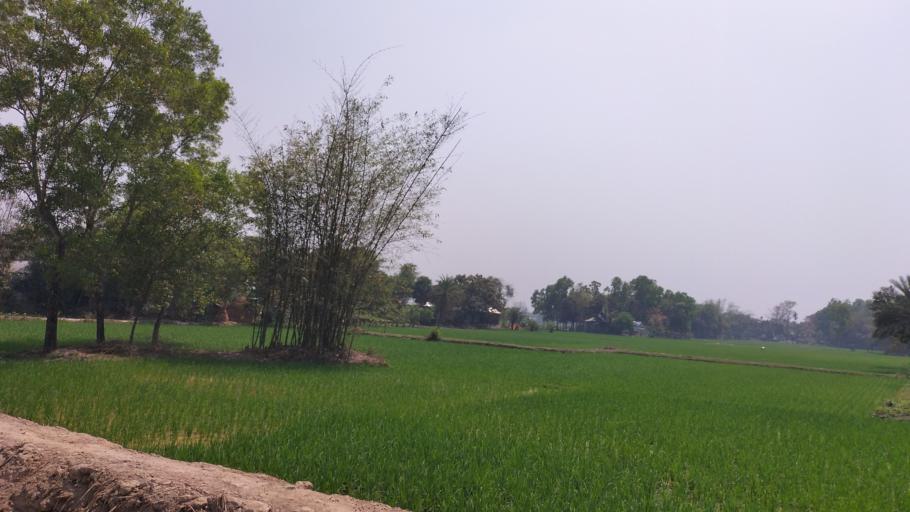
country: BD
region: Dhaka
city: Sakhipur
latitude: 24.3074
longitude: 90.3037
